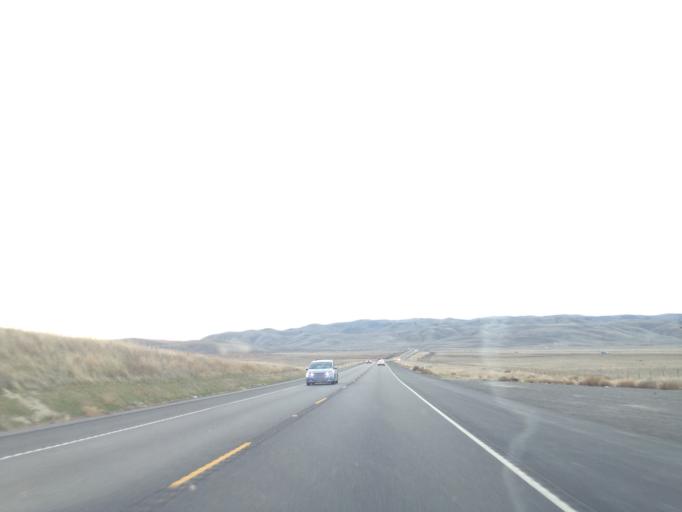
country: US
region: California
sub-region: San Luis Obispo County
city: Shandon
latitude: 35.7380
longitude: -120.2668
